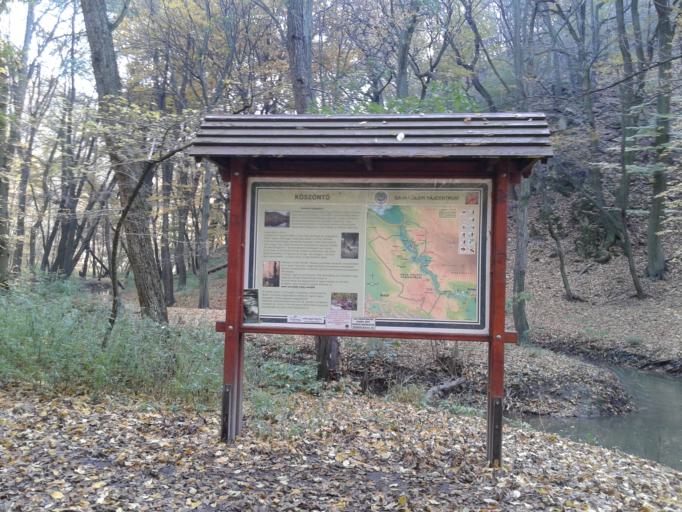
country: HU
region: Fejer
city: Bodajk
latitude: 47.3142
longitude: 18.2153
